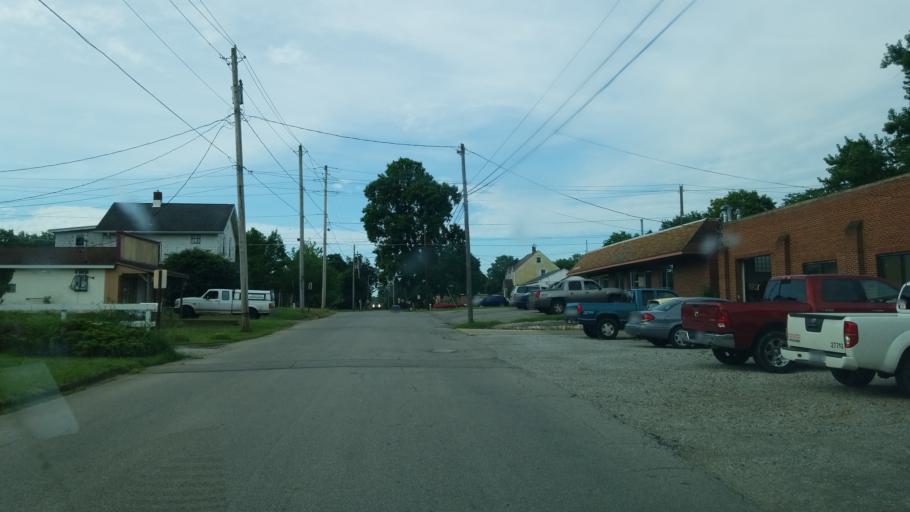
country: US
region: Ohio
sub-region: Ashland County
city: Ashland
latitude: 40.8736
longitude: -82.2962
